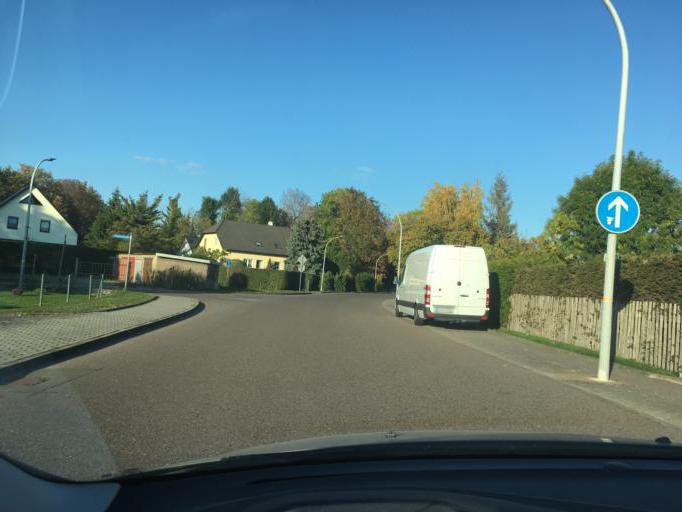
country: DE
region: Saxony-Anhalt
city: Lutzen
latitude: 51.2534
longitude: 12.1438
